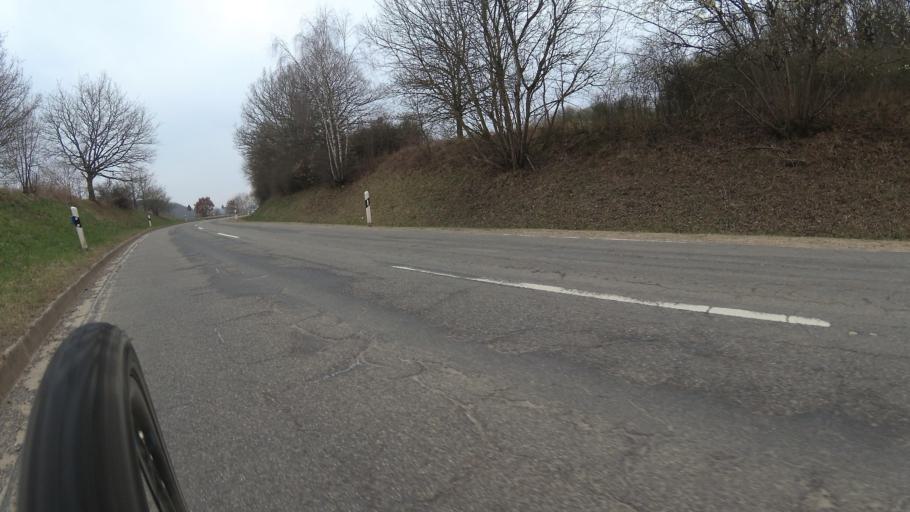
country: DE
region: Rheinland-Pfalz
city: Dienstweiler
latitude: 49.6349
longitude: 7.1939
